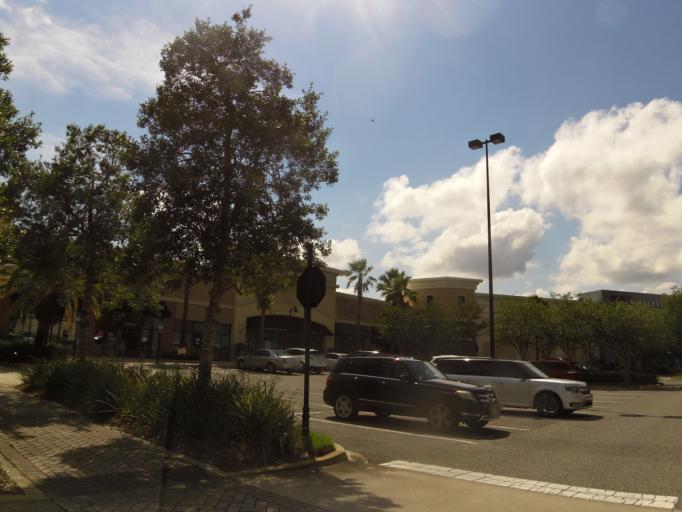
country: US
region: Florida
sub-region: Duval County
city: Jacksonville Beach
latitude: 30.2530
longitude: -81.5313
